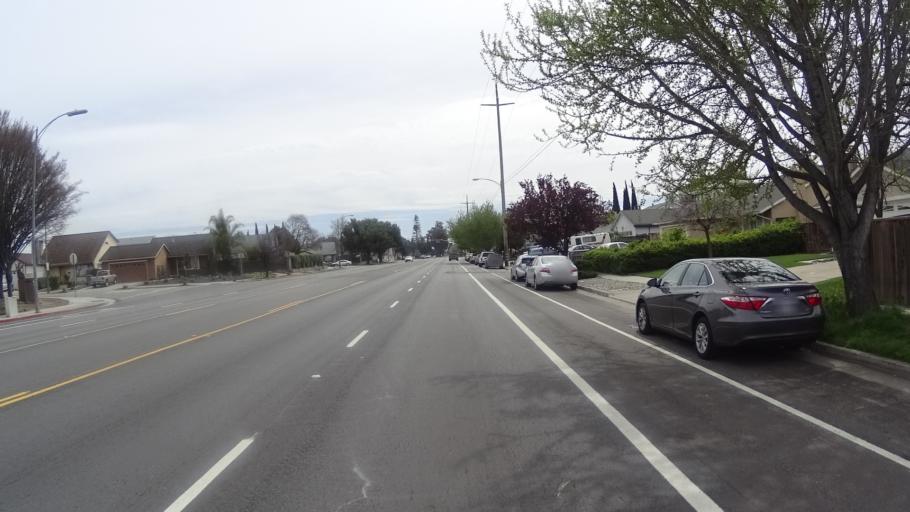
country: US
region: California
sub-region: Santa Clara County
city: San Jose
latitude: 37.3869
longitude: -121.8749
